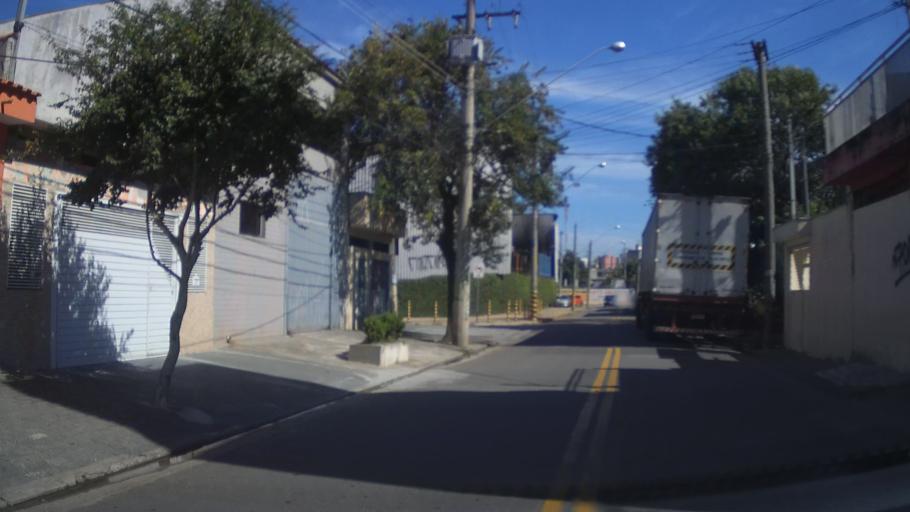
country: BR
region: Sao Paulo
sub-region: Sao Caetano Do Sul
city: Sao Caetano do Sul
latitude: -23.6493
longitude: -46.5658
